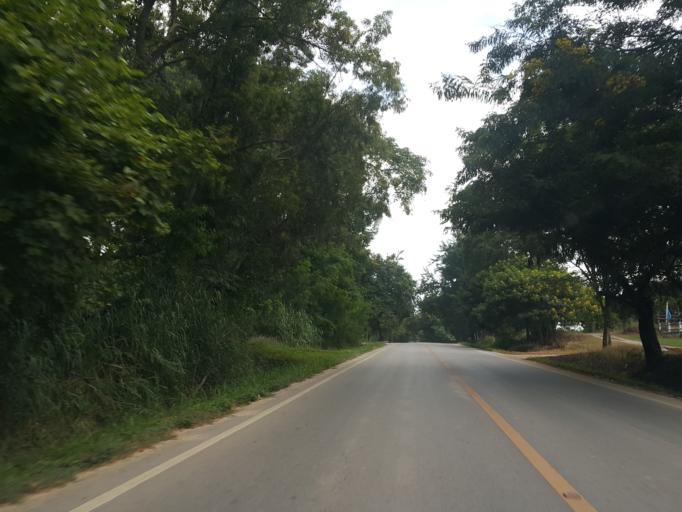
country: TH
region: Chiang Mai
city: Phrao
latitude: 19.3019
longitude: 99.1892
